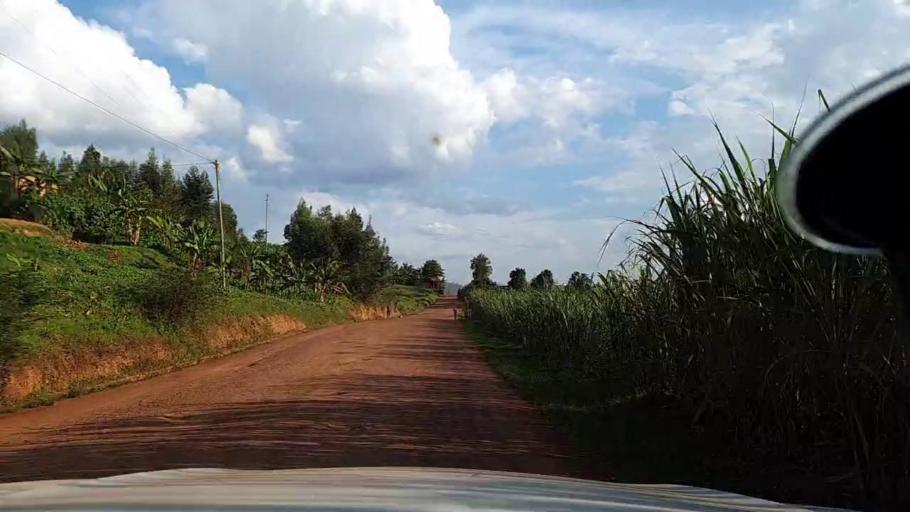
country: RW
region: Kigali
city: Kigali
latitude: -1.9245
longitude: 29.9903
